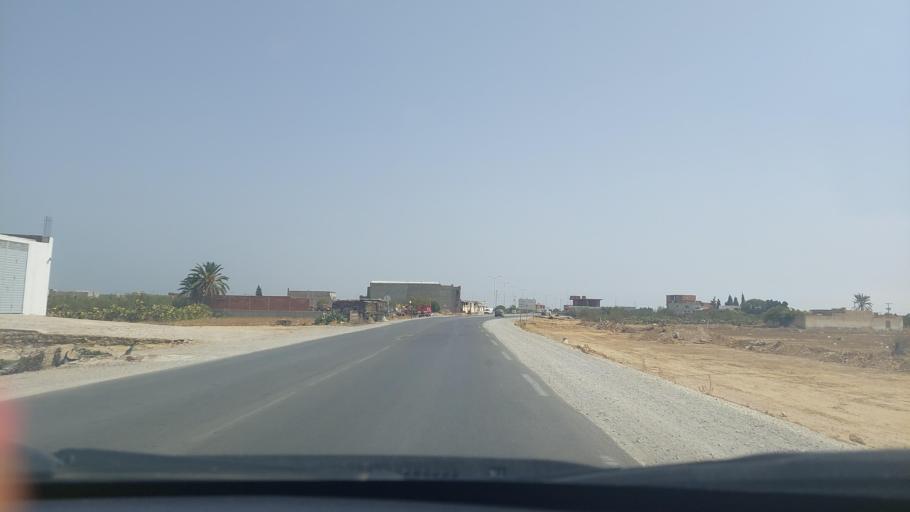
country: TN
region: Al Munastir
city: Qasr Hallal
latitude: 35.6046
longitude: 10.8871
